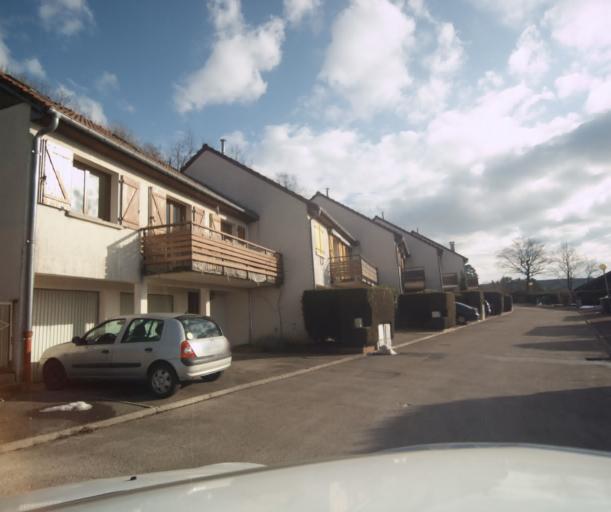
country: FR
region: Franche-Comte
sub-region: Departement du Doubs
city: Besancon
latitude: 47.2602
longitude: 6.0515
